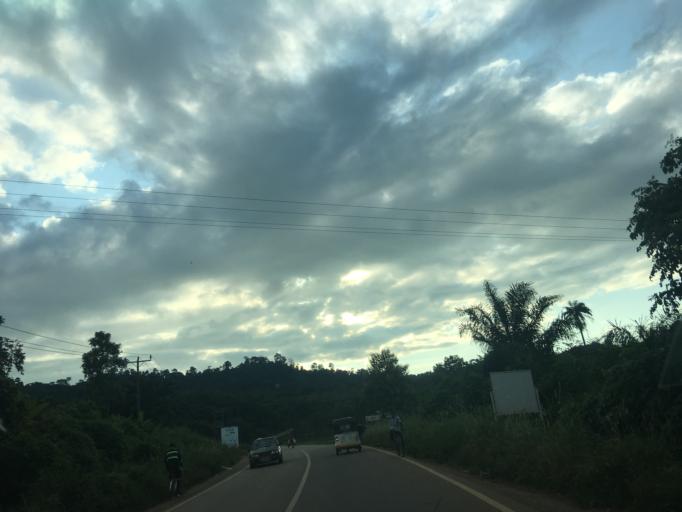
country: GH
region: Western
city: Bibiani
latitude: 6.4637
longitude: -2.3243
